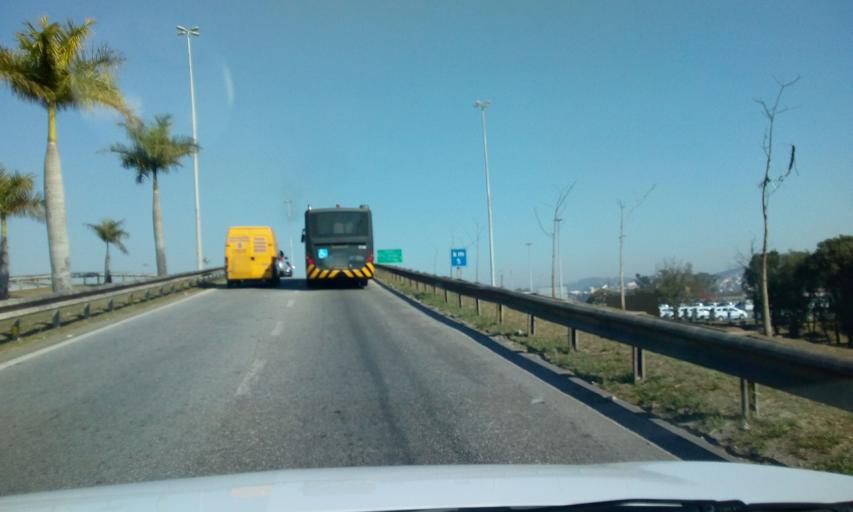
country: BR
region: Sao Paulo
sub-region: Guarulhos
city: Guarulhos
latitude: -23.4217
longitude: -46.4793
